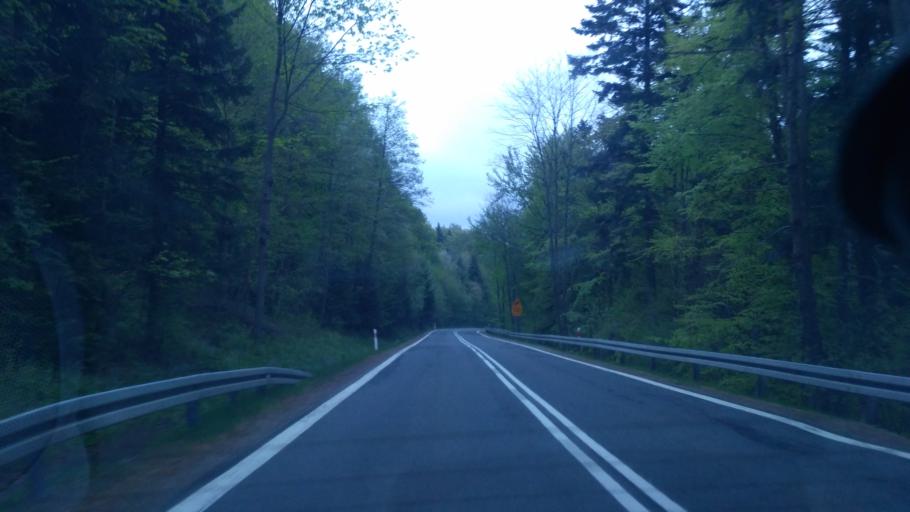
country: PL
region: Subcarpathian Voivodeship
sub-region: Powiat sanocki
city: Tyrawa Woloska
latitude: 49.5612
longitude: 22.3396
